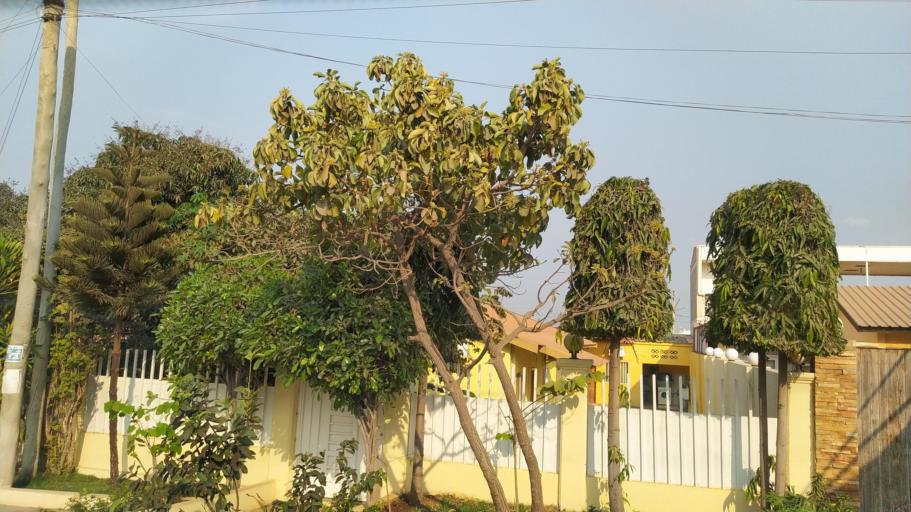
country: AO
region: Luanda
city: Luanda
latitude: -8.9119
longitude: 13.2253
